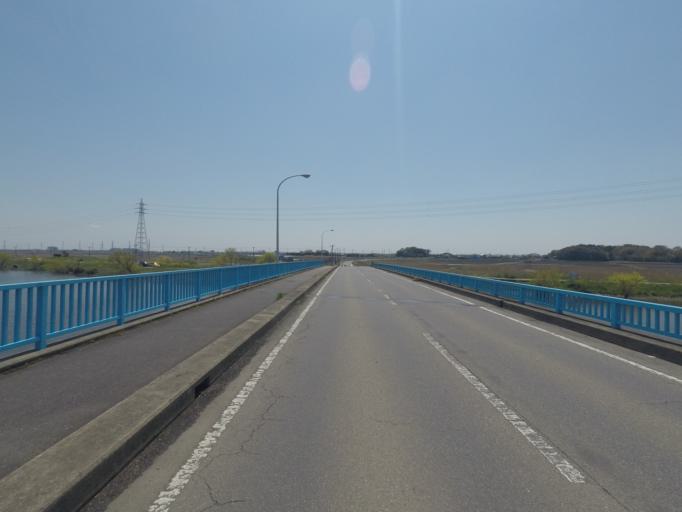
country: JP
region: Ibaraki
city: Ushiku
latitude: 35.9544
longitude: 140.1030
